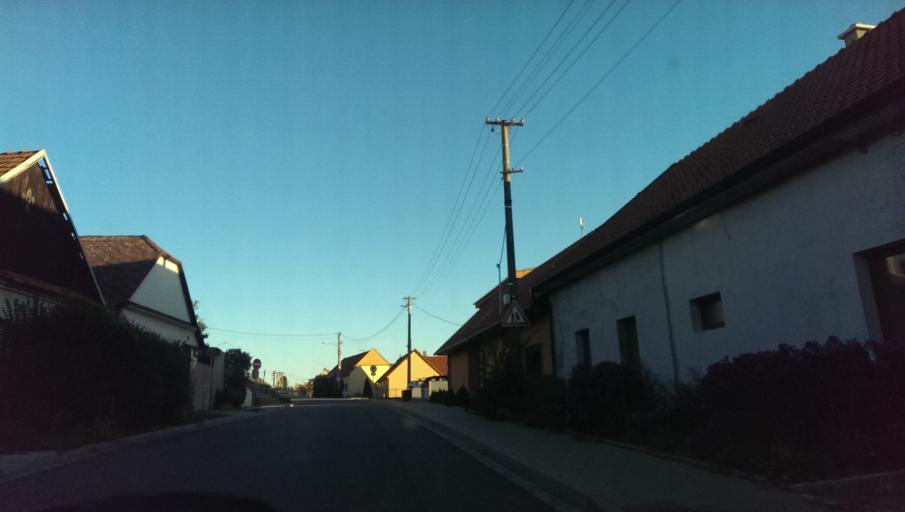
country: CZ
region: Zlin
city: Tupesy
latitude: 49.0845
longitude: 17.3727
